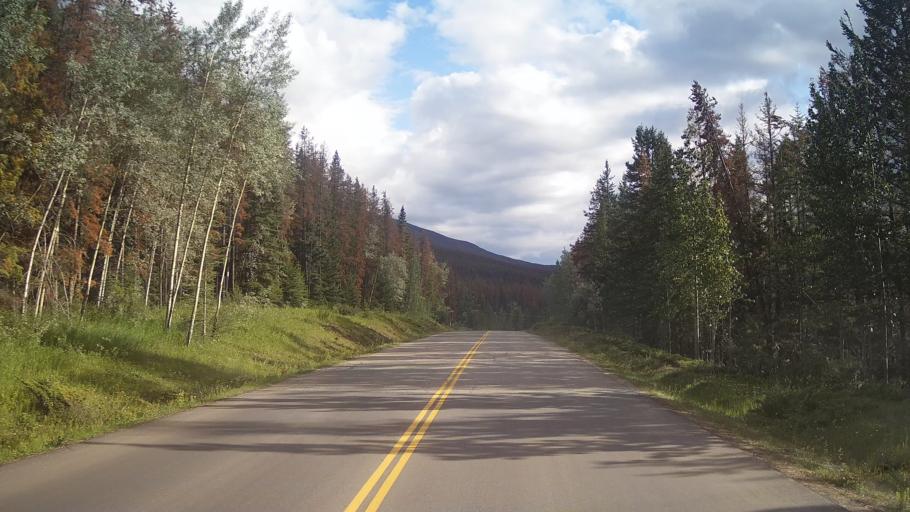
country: CA
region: Alberta
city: Jasper Park Lodge
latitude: 52.9173
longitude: -118.0014
